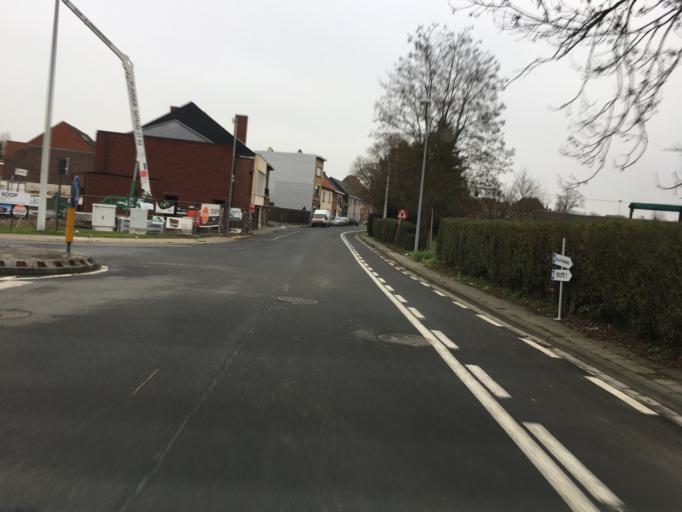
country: BE
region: Flanders
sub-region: Provincie West-Vlaanderen
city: Menen
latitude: 50.7934
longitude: 3.1081
